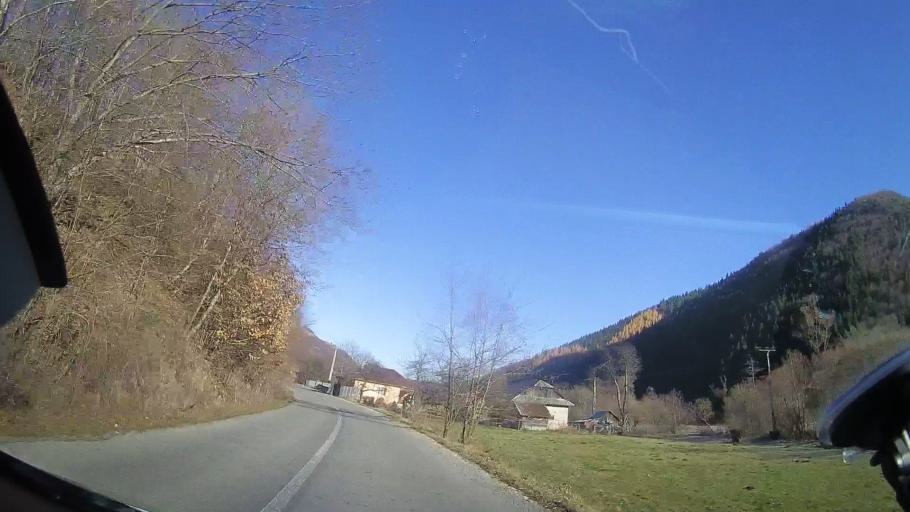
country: RO
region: Cluj
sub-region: Comuna Sacueu
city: Sacuieu
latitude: 46.8551
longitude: 22.8641
